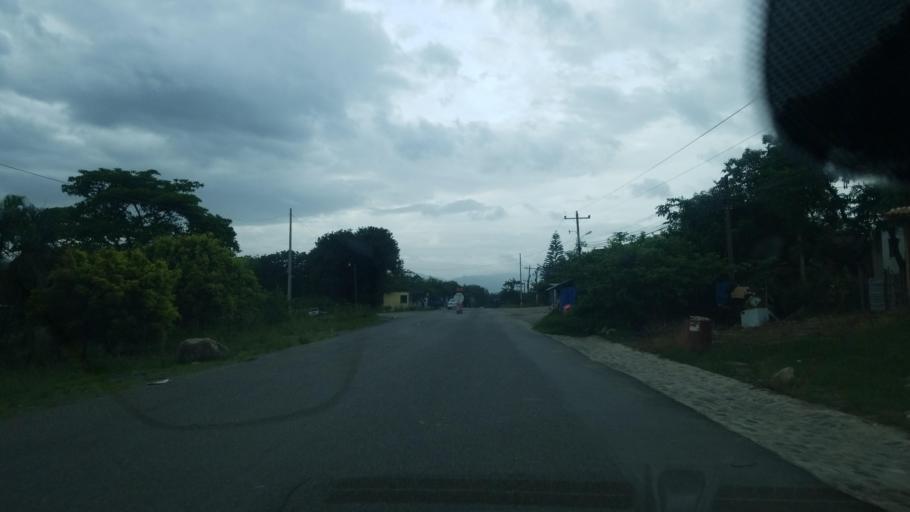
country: HN
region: Ocotepeque
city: Antigua Ocotepeque
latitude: 14.3792
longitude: -89.2086
